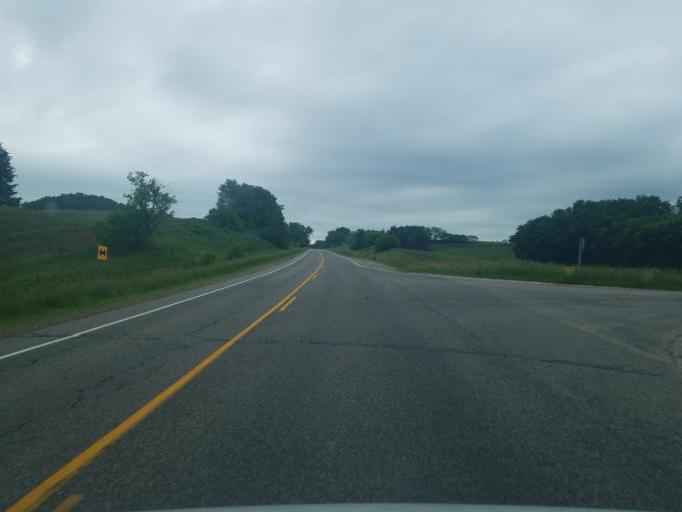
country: US
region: Wisconsin
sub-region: Juneau County
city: Elroy
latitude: 43.7754
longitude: -90.2052
